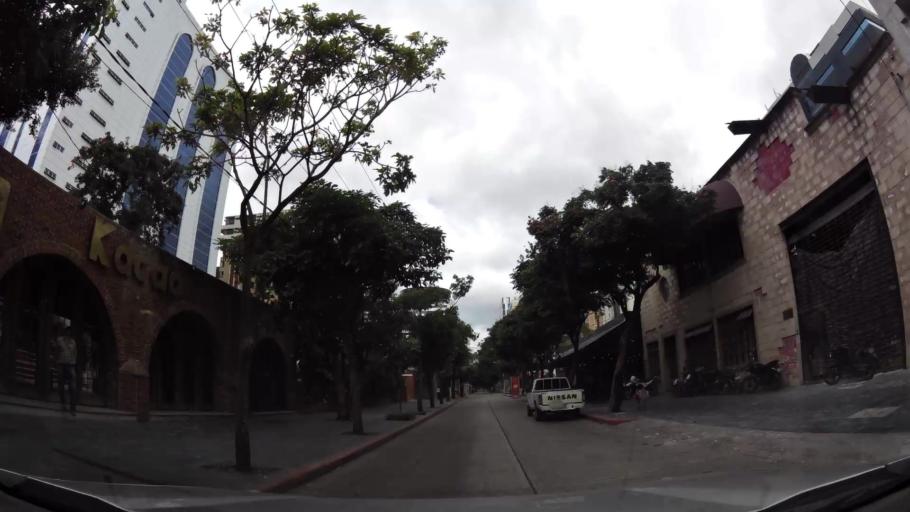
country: GT
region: Guatemala
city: Santa Catarina Pinula
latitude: 14.5986
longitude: -90.5148
